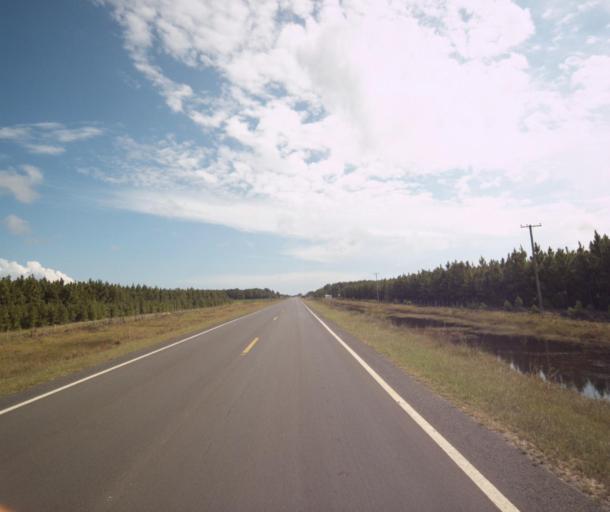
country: BR
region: Rio Grande do Sul
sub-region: Sao Lourenco Do Sul
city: Sao Lourenco do Sul
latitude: -31.5973
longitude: -51.3762
